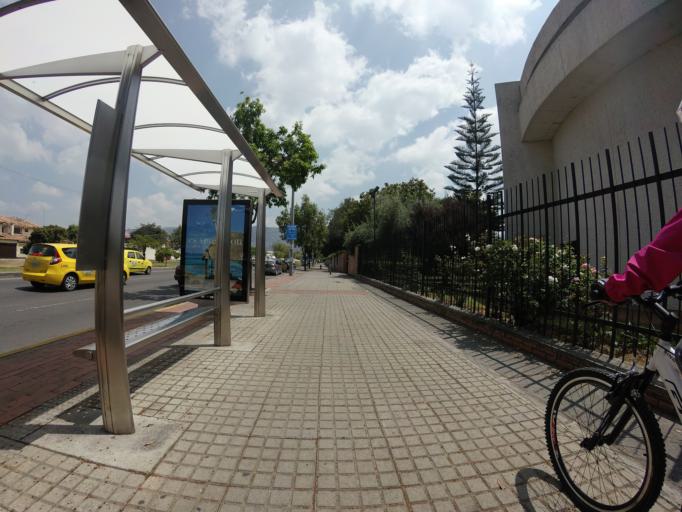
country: CO
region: Bogota D.C.
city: Barrio San Luis
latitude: 4.7366
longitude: -74.0448
